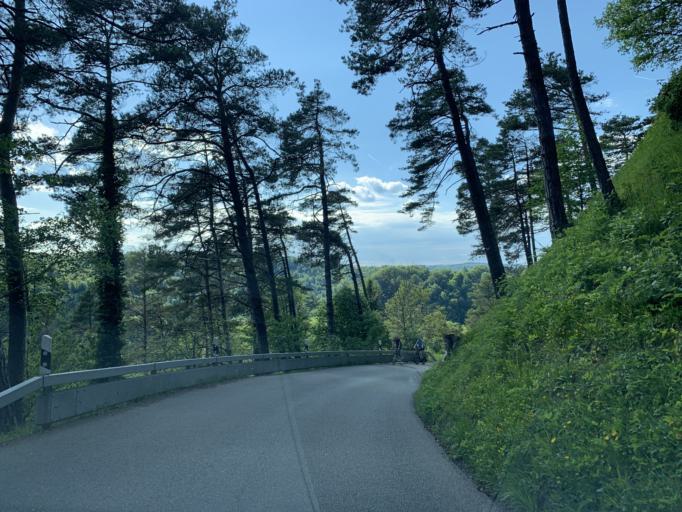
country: CH
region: Zurich
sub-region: Bezirk Winterthur
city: Mattenbach (Kreis 7)
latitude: 47.4595
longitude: 8.7411
